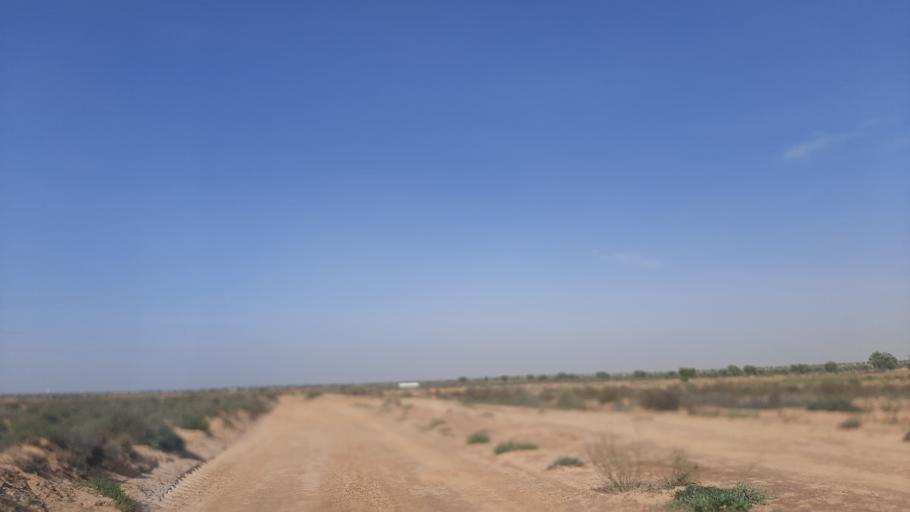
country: TN
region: Madanin
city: Zarzis
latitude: 33.4467
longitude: 10.8079
